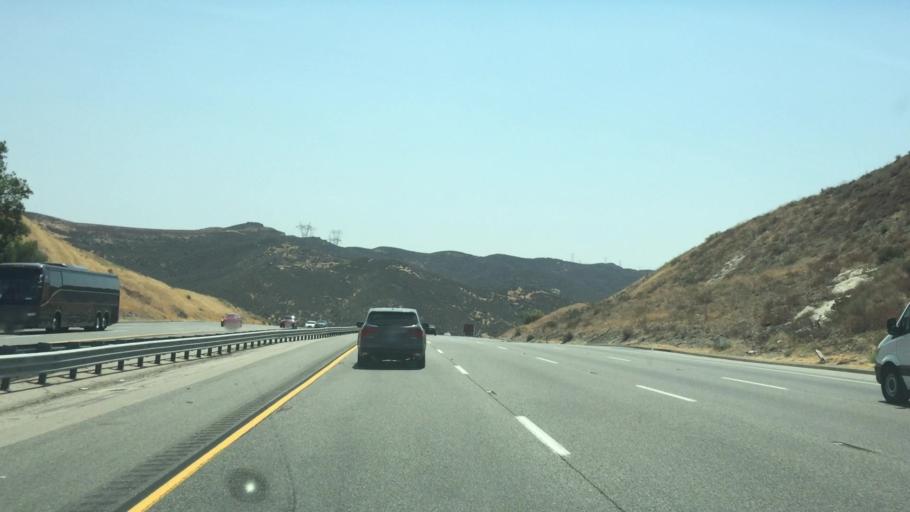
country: US
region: California
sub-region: Los Angeles County
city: Castaic
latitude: 34.6275
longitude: -118.7235
